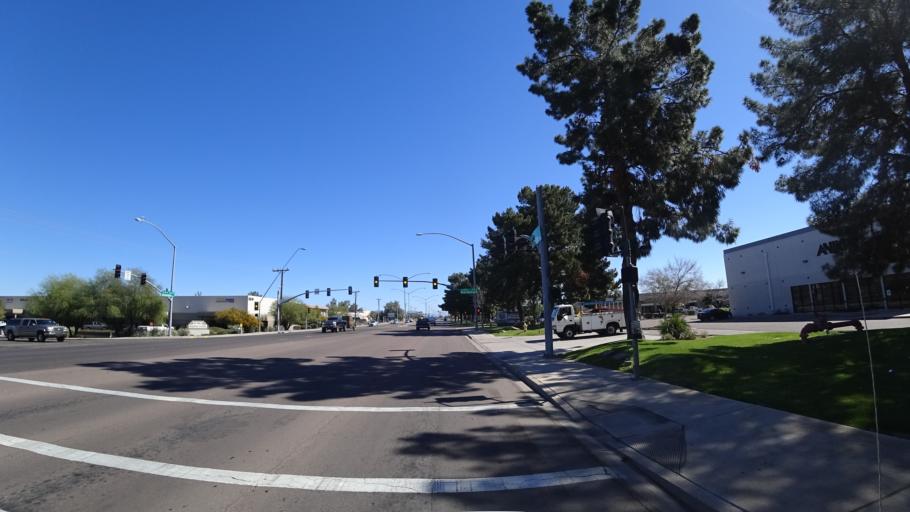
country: US
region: Arizona
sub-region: Maricopa County
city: San Carlos
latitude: 33.3787
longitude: -111.8343
